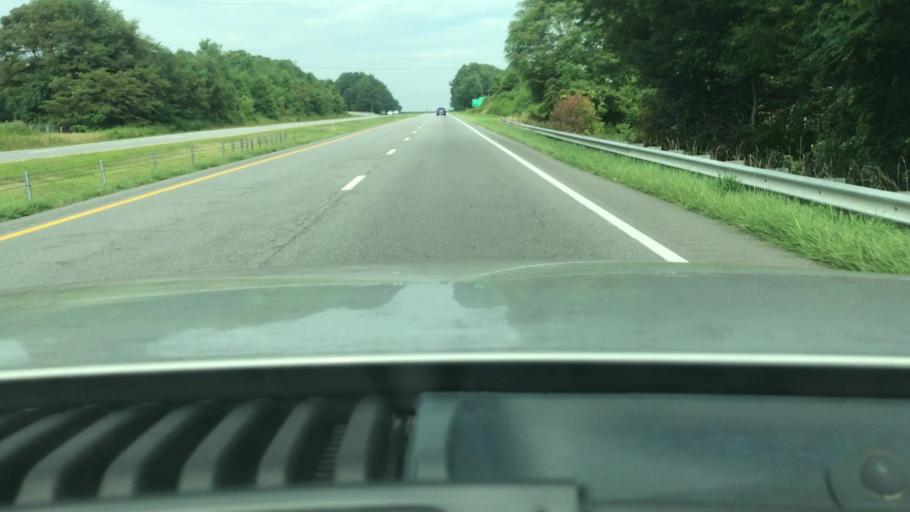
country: US
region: North Carolina
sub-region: Wilkes County
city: North Wilkesboro
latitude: 36.1509
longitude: -81.0102
